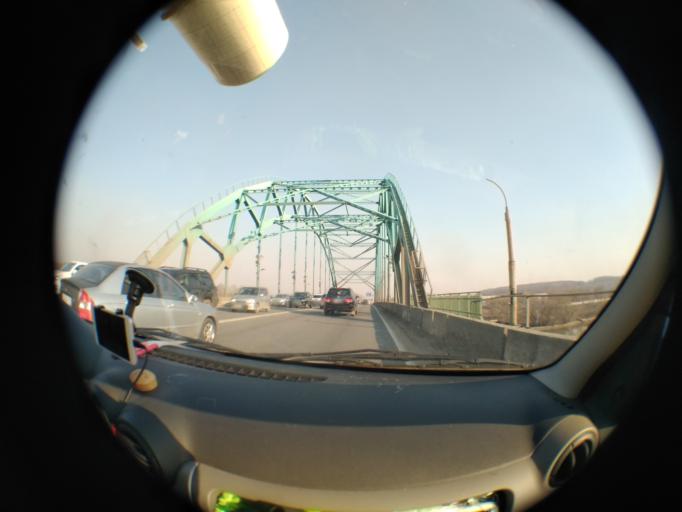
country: RU
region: Moskovskaya
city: Ostrovtsy
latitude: 55.5698
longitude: 38.0342
